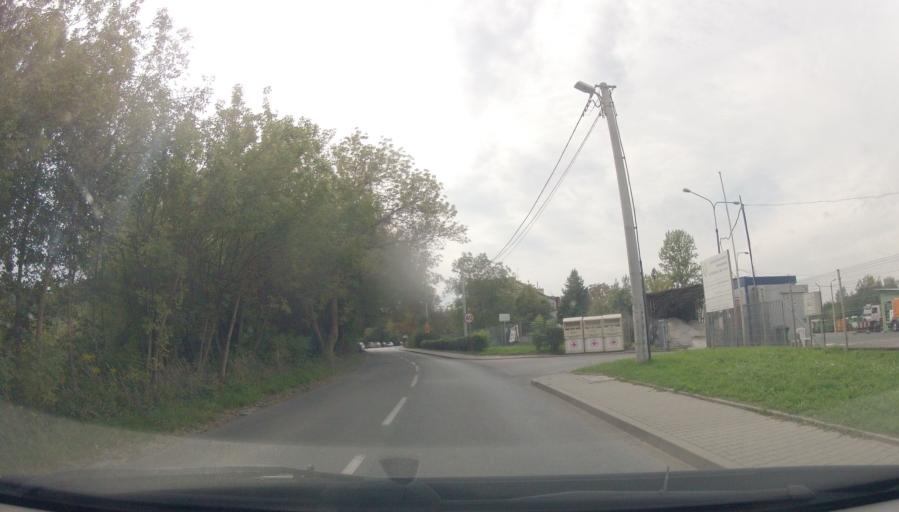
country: PL
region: Lesser Poland Voivodeship
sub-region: Powiat wielicki
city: Wieliczka
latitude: 49.9837
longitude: 20.0393
